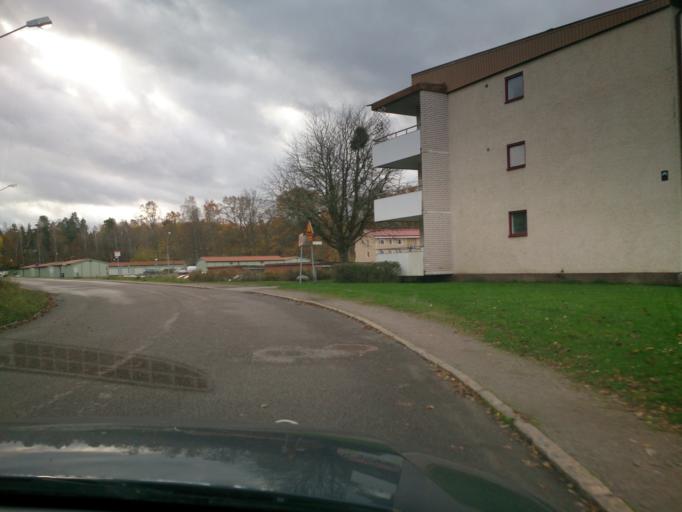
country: SE
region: OEstergoetland
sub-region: Atvidabergs Kommun
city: Atvidaberg
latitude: 58.1911
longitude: 16.0097
